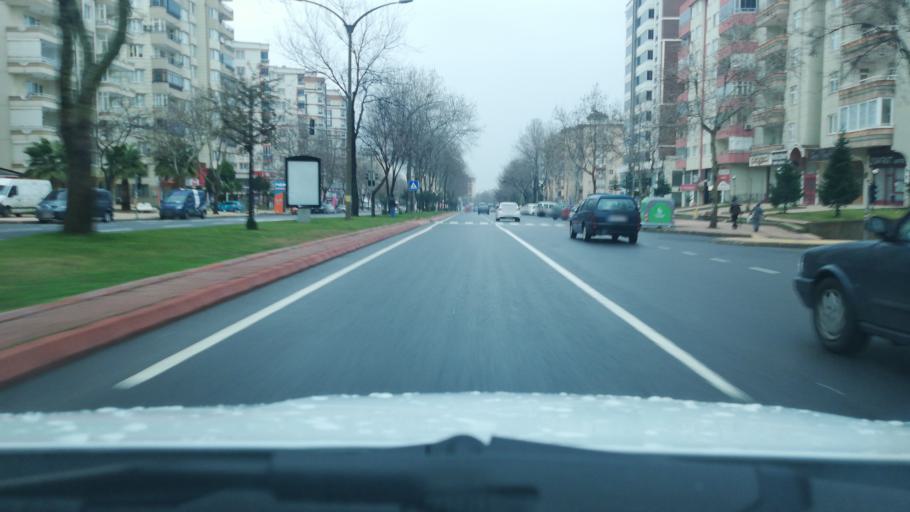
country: TR
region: Kahramanmaras
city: Kahramanmaras
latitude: 37.5873
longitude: 36.8934
